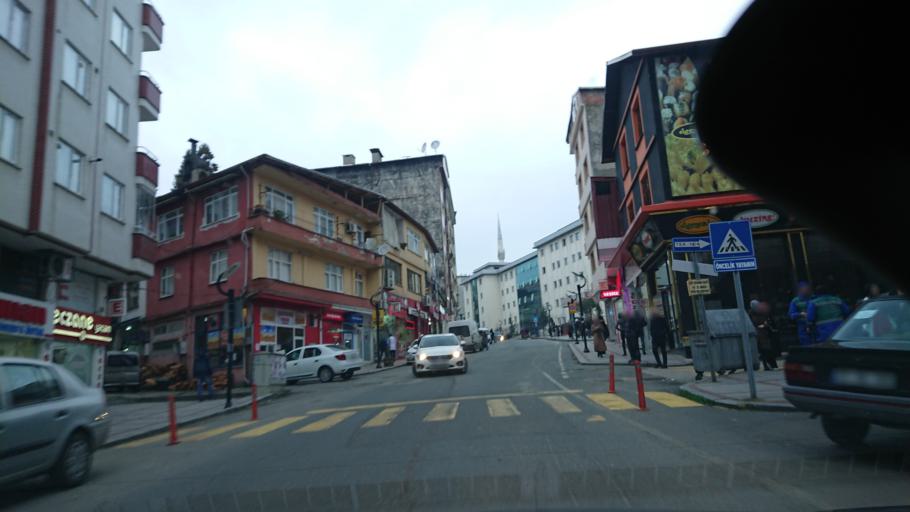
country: TR
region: Rize
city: Rize
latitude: 41.0271
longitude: 40.5144
